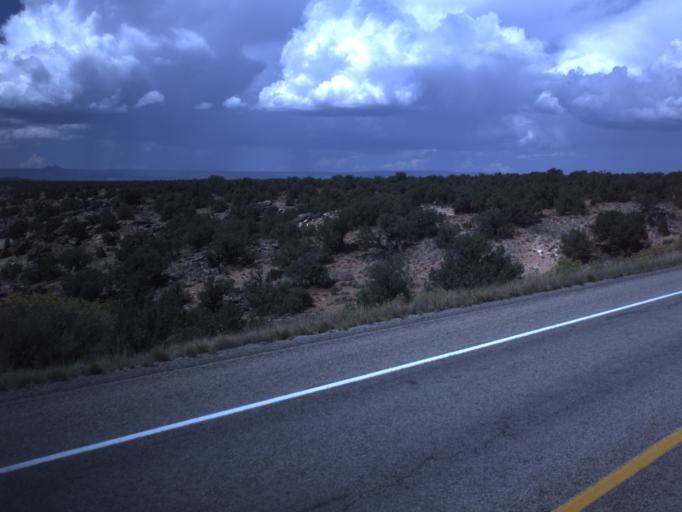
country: US
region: Utah
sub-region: San Juan County
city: Blanding
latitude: 37.4755
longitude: -109.4673
